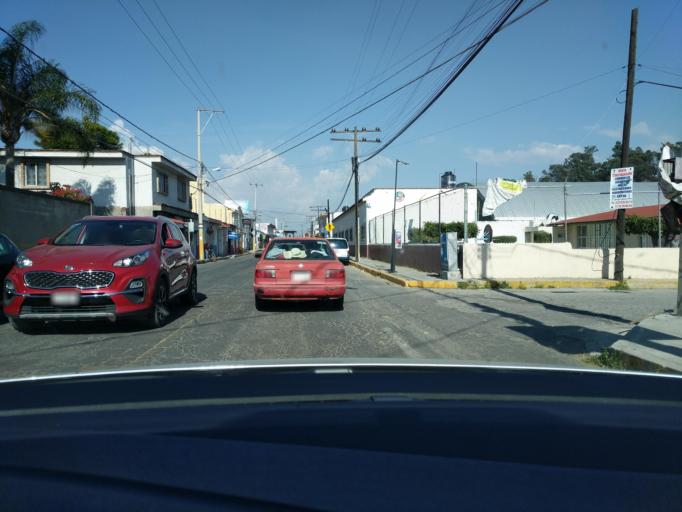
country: MX
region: Puebla
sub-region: San Gregorio Atzompa
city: Chipilo de Francisco Javier Mina
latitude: 19.0044
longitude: -98.3345
